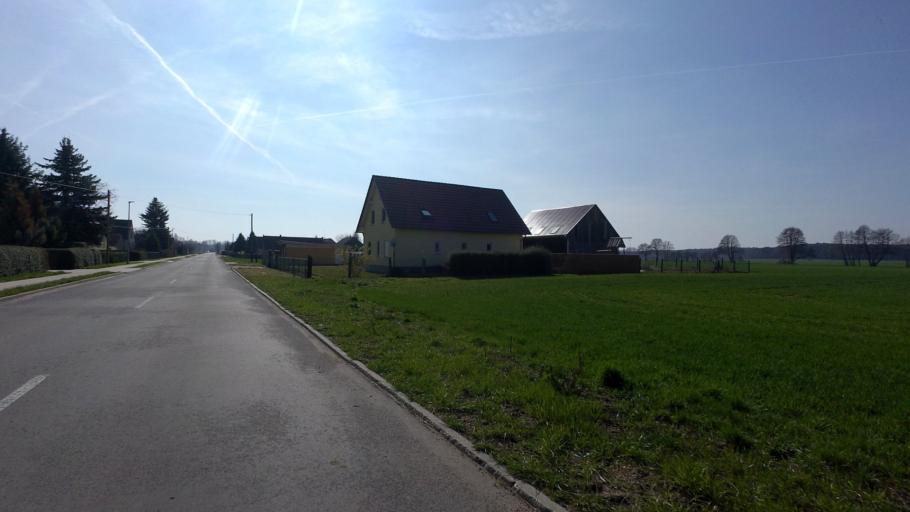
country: DE
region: Brandenburg
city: Drahnsdorf
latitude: 51.9325
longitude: 13.5951
